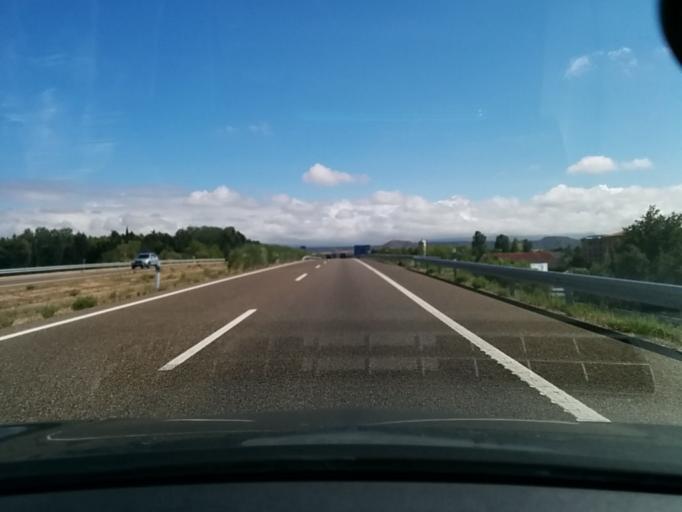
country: ES
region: Aragon
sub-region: Provincia de Huesca
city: Huesca
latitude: 42.1475
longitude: -0.4277
